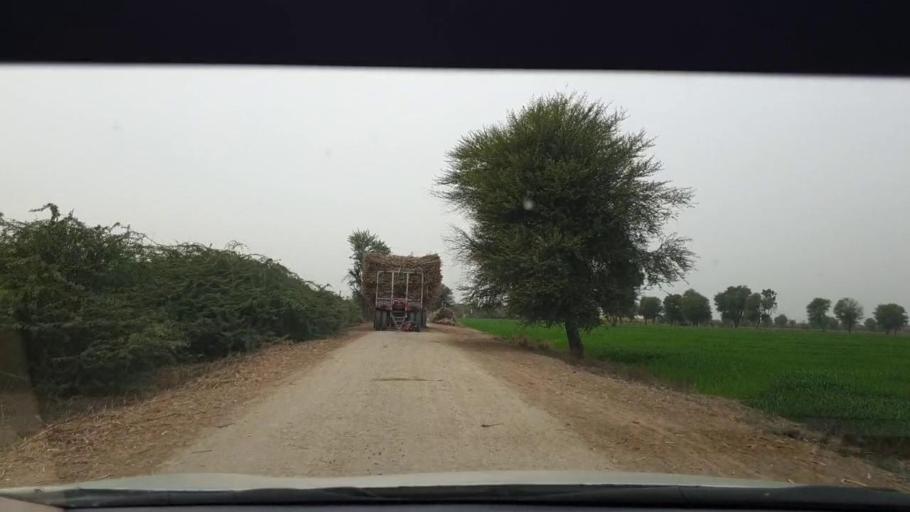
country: PK
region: Sindh
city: Berani
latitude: 25.8837
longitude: 68.7976
